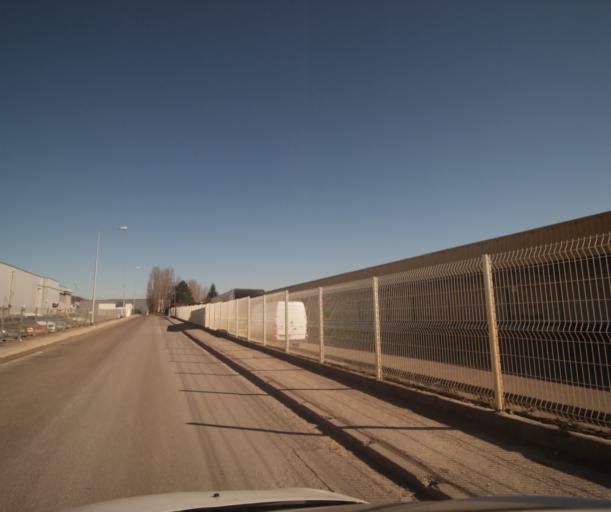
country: FR
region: Franche-Comte
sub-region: Departement du Doubs
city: Pirey
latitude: 47.2400
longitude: 5.9846
